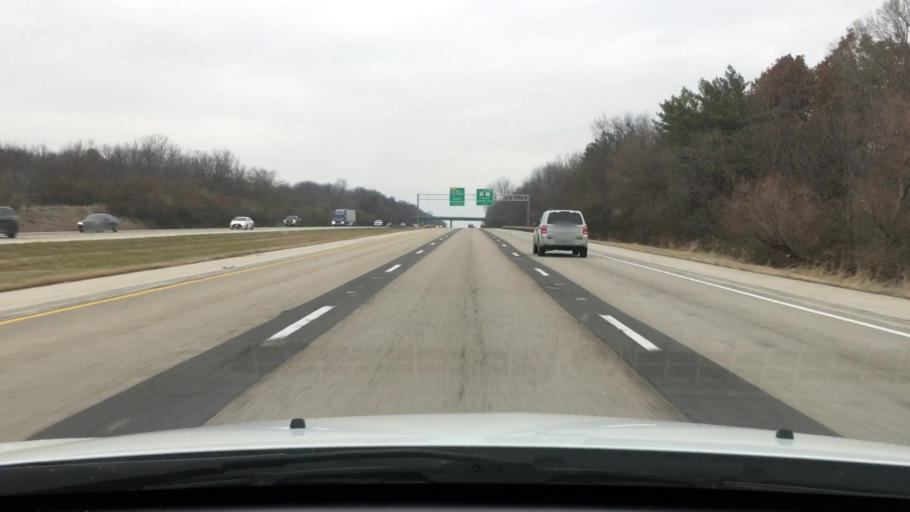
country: US
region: Illinois
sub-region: Logan County
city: Lincoln
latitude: 40.1410
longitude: -89.4170
